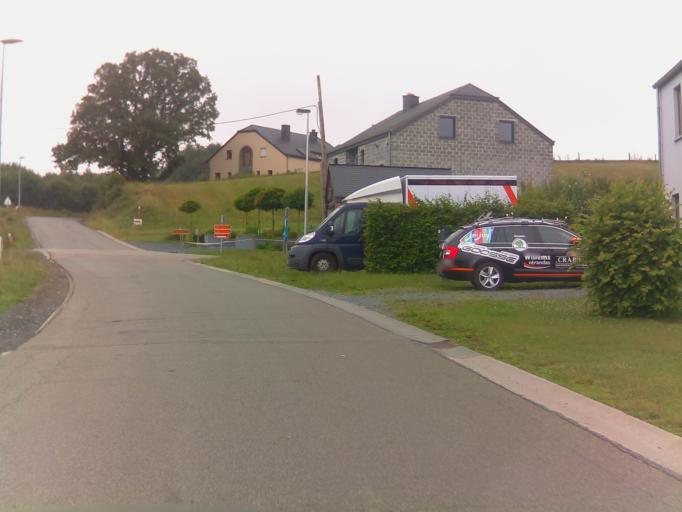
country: BE
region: Wallonia
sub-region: Province du Luxembourg
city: Leglise
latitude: 49.7984
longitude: 5.5396
